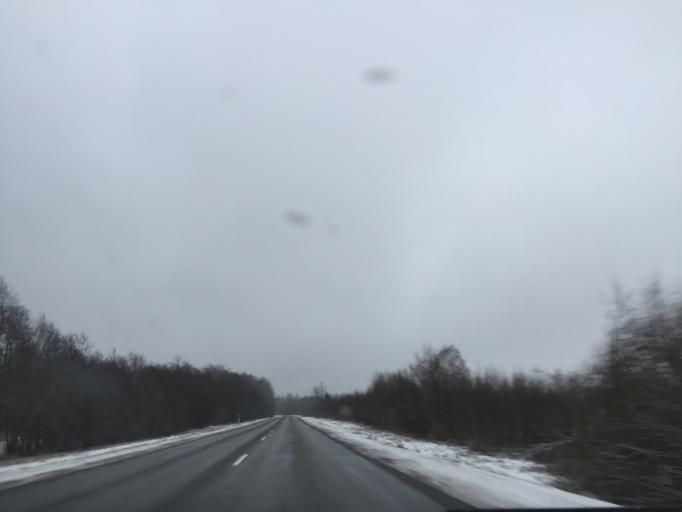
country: EE
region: Laeaene
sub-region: Lihula vald
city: Lihula
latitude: 58.5562
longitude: 23.9866
